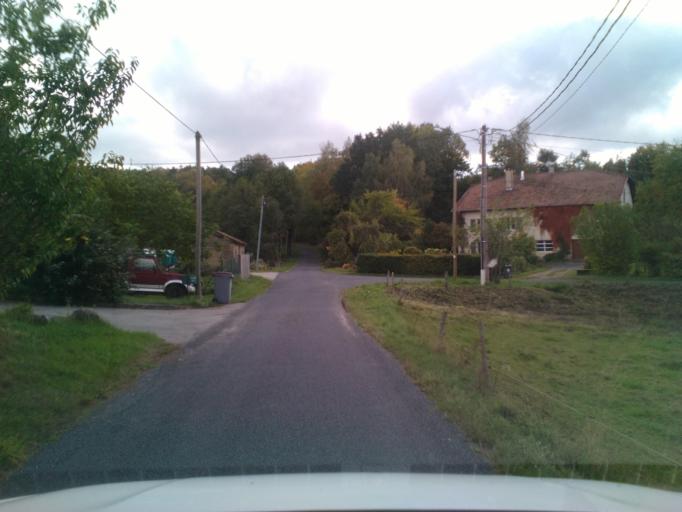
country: FR
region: Lorraine
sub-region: Departement des Vosges
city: Senones
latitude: 48.3531
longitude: 7.0208
